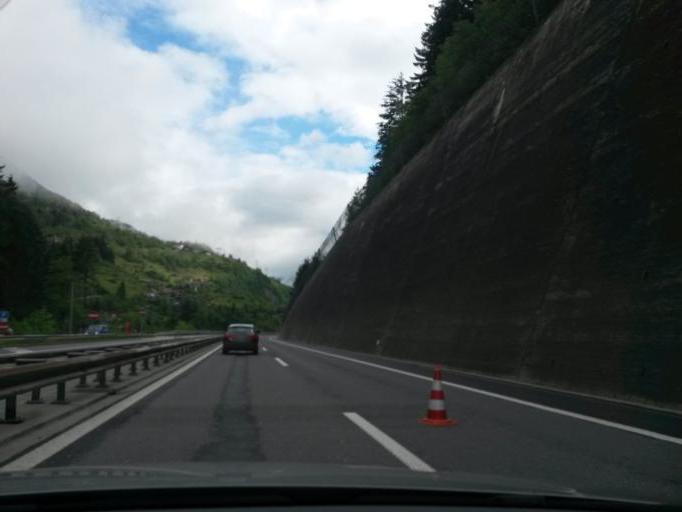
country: CH
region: Uri
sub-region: Uri
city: Silenen
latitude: 46.7212
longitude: 8.6186
